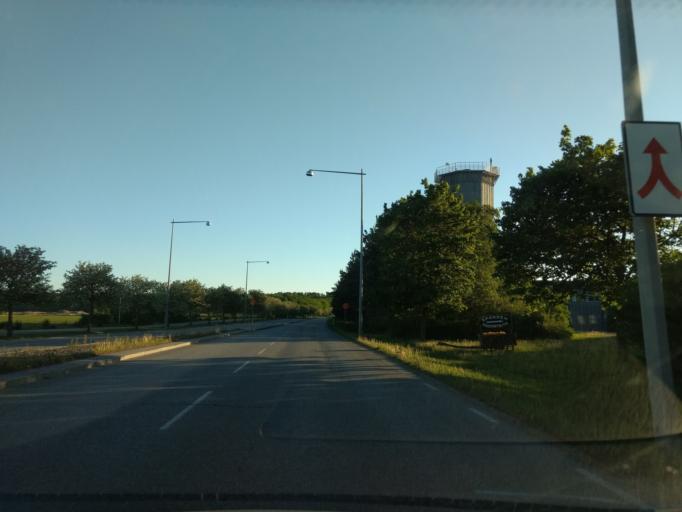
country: SE
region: Uppsala
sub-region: Uppsala Kommun
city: Uppsala
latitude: 59.8444
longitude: 17.6653
